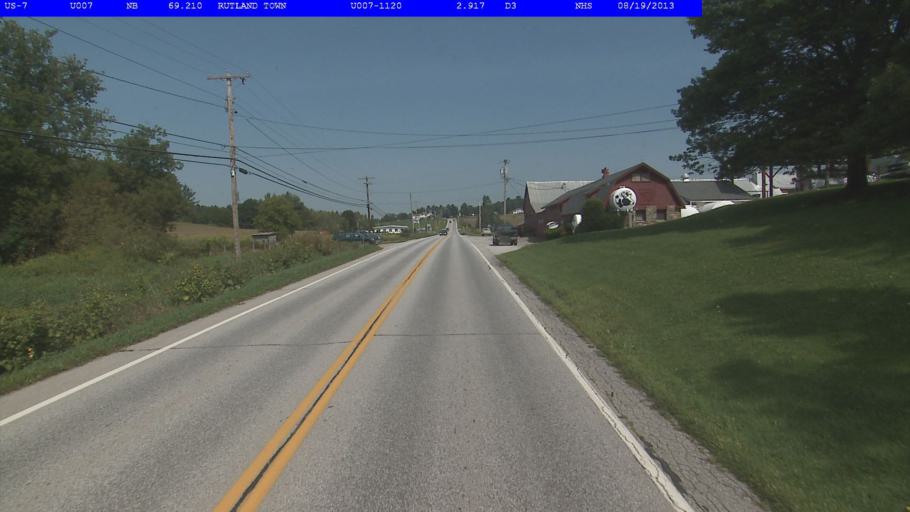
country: US
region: Vermont
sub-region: Rutland County
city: Rutland
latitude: 43.6527
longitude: -72.9861
